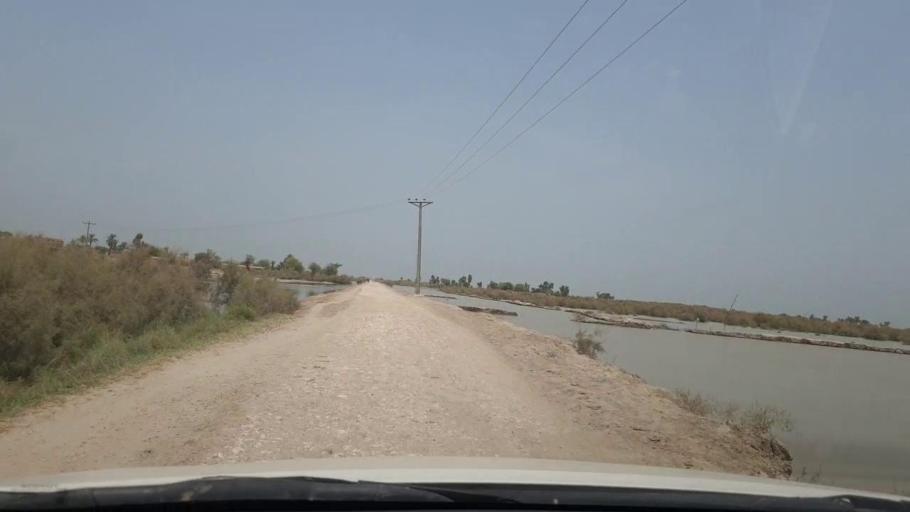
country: PK
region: Sindh
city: Rustam jo Goth
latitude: 28.0541
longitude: 68.8159
